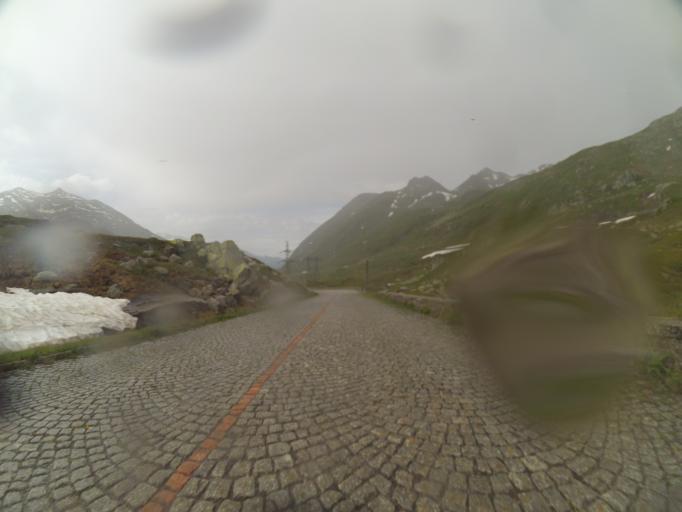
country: CH
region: Ticino
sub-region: Leventina District
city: Airolo
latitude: 46.5638
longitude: 8.5572
